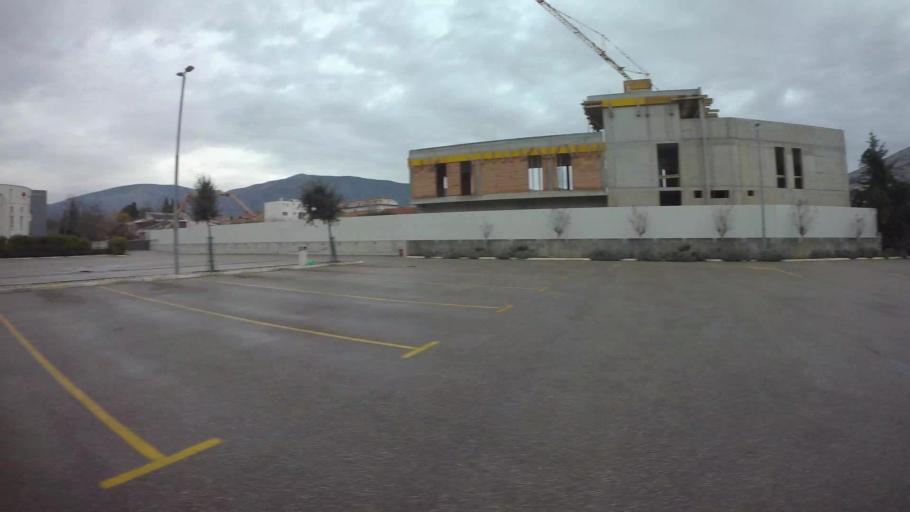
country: BA
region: Federation of Bosnia and Herzegovina
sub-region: Hercegovacko-Bosanski Kanton
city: Mostar
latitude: 43.3386
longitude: 17.8087
